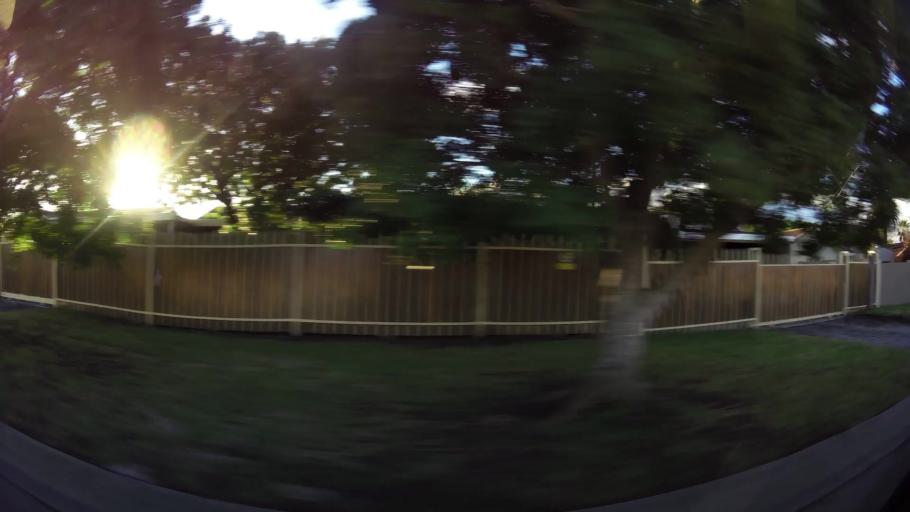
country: ZA
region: Eastern Cape
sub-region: Nelson Mandela Bay Metropolitan Municipality
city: Port Elizabeth
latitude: -33.9735
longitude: 25.4961
